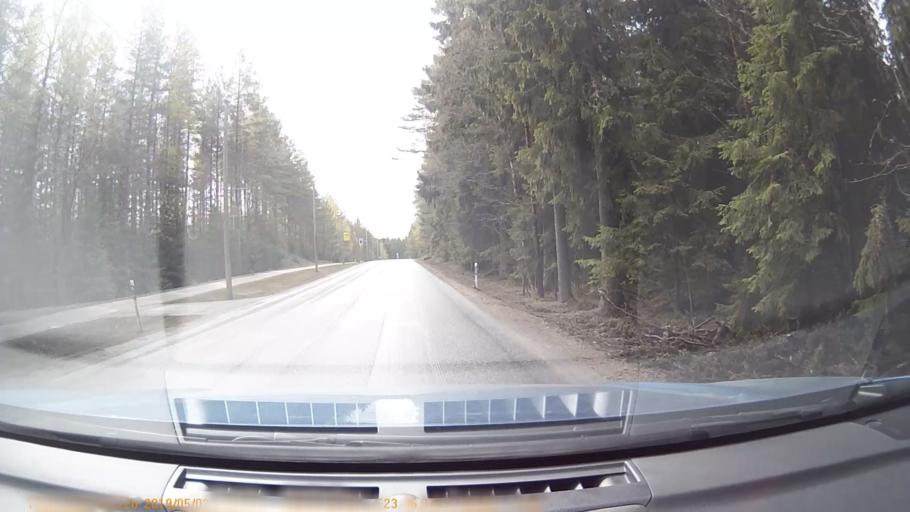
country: FI
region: Pirkanmaa
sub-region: Tampere
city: Yloejaervi
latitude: 61.5413
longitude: 23.6012
